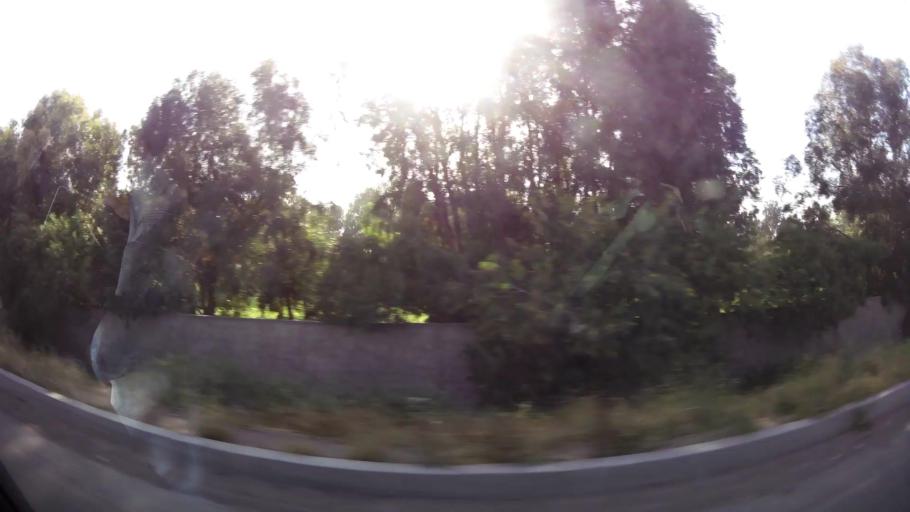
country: MA
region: Souss-Massa-Draa
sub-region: Inezgane-Ait Mellou
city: Inezgane
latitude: 30.3556
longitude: -9.5059
